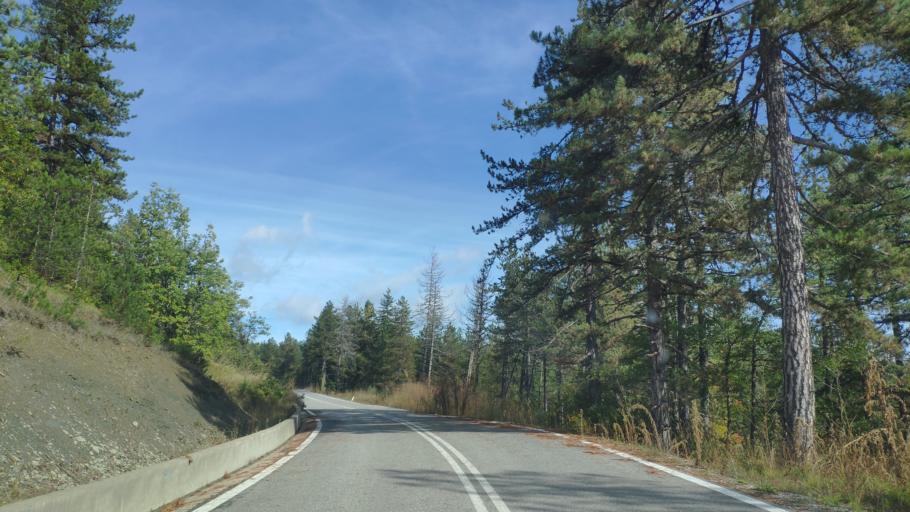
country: AL
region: Korce
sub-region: Rrethi i Devollit
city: Miras
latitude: 40.3679
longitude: 20.9256
